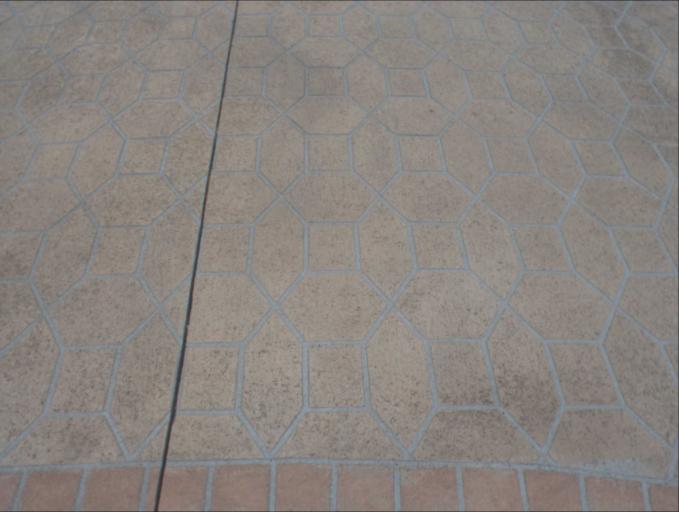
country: AU
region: Queensland
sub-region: Logan
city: Windaroo
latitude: -27.7388
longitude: 153.1915
